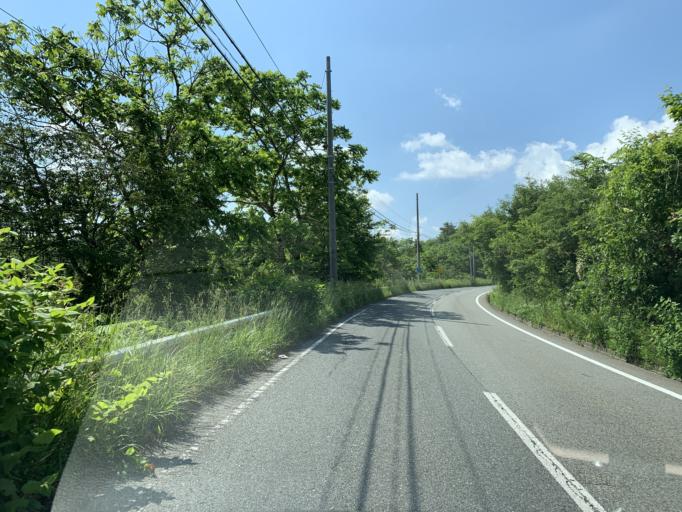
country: JP
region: Miyagi
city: Furukawa
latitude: 38.7193
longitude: 140.9487
